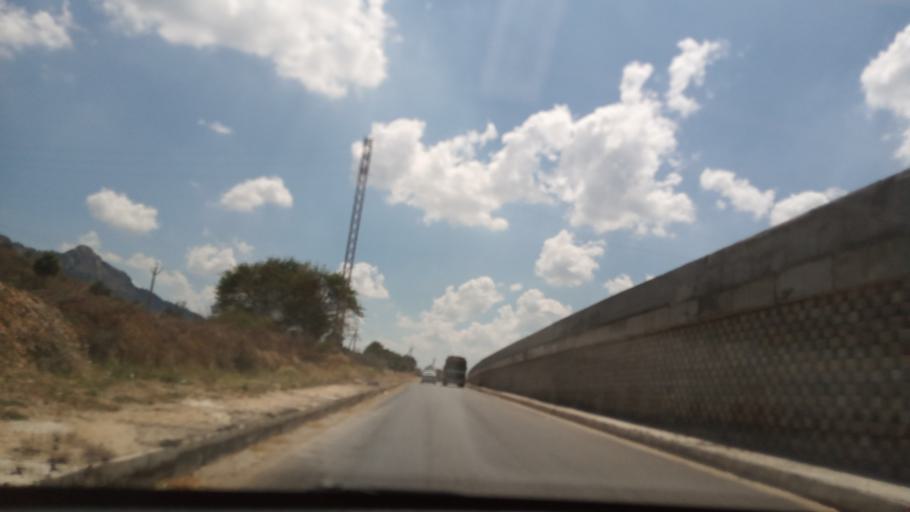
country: IN
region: Andhra Pradesh
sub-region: Chittoor
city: Pakala
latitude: 13.3369
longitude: 79.0793
